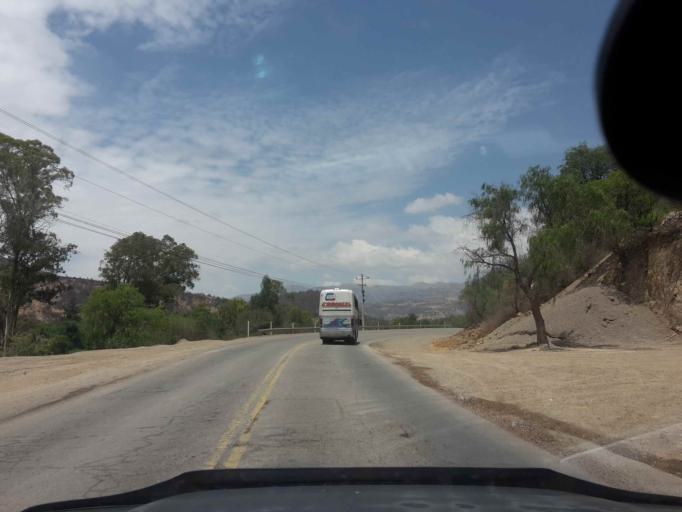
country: BO
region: Cochabamba
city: Sipe Sipe
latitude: -17.5422
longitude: -66.3364
